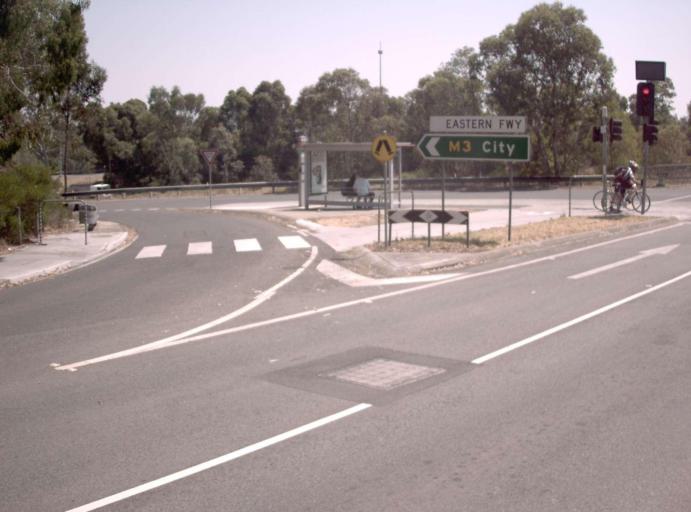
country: AU
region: Victoria
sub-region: Manningham
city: Bulleen
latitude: -37.7812
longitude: 145.0785
